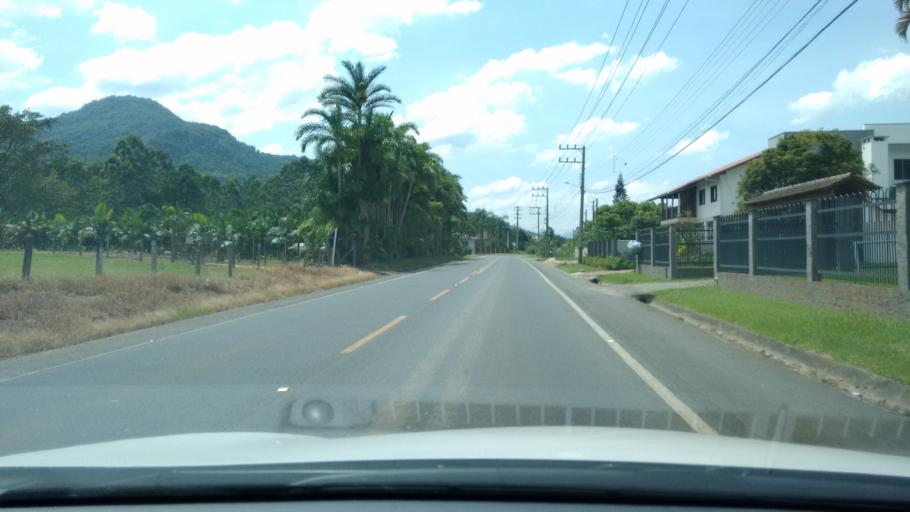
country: BR
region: Santa Catarina
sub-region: Timbo
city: Timbo
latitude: -26.8340
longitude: -49.3230
